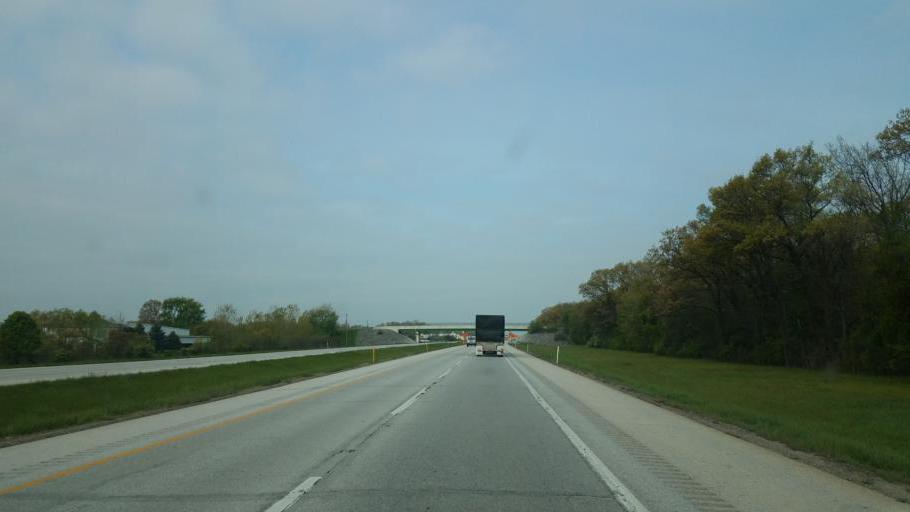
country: US
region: Indiana
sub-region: Elkhart County
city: Simonton Lake
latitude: 41.7293
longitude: -85.9092
